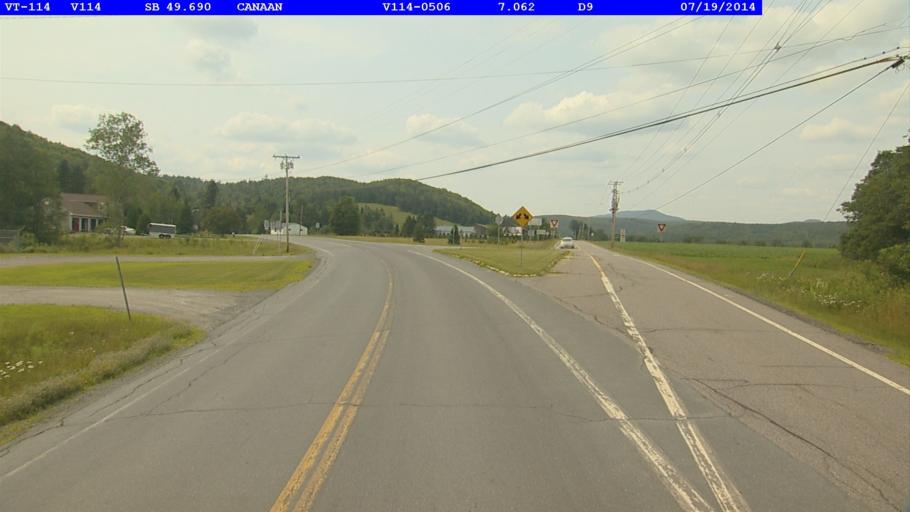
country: US
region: New Hampshire
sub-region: Coos County
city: Colebrook
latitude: 45.0065
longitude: -71.5554
